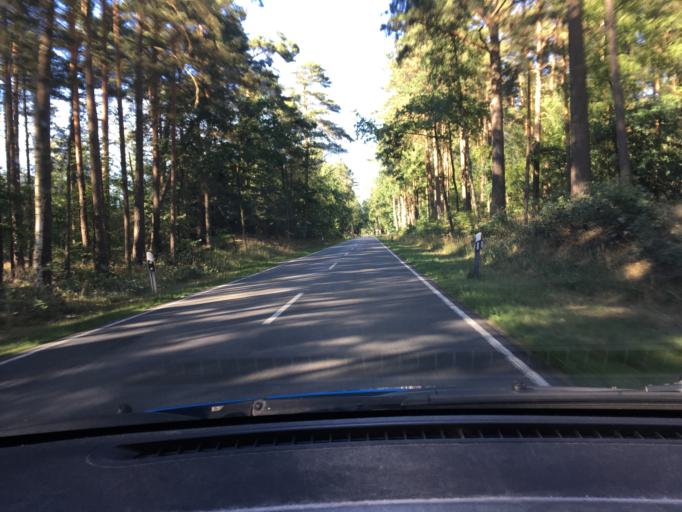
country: DE
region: Lower Saxony
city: Neetze
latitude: 53.2863
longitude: 10.6466
